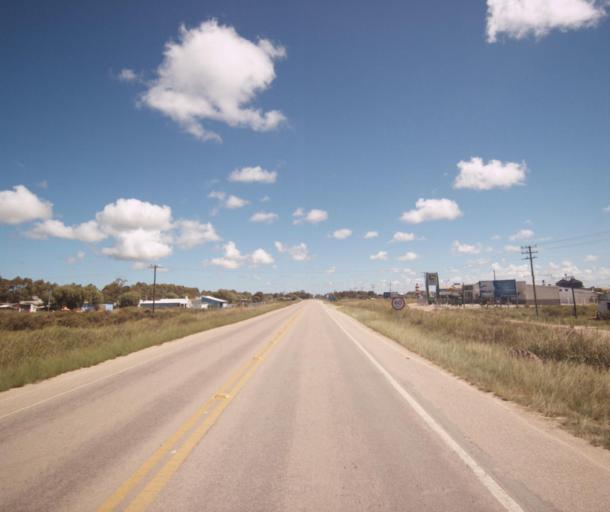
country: BR
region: Rio Grande do Sul
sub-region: Santa Vitoria Do Palmar
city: Santa Vitoria do Palmar
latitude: -33.5285
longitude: -53.3433
